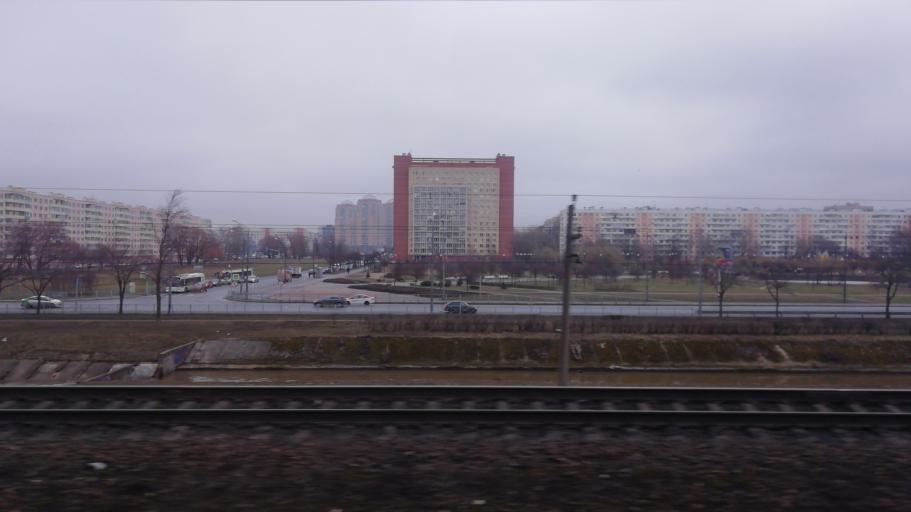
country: RU
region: St.-Petersburg
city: Kupchino
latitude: 59.8656
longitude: 30.3586
